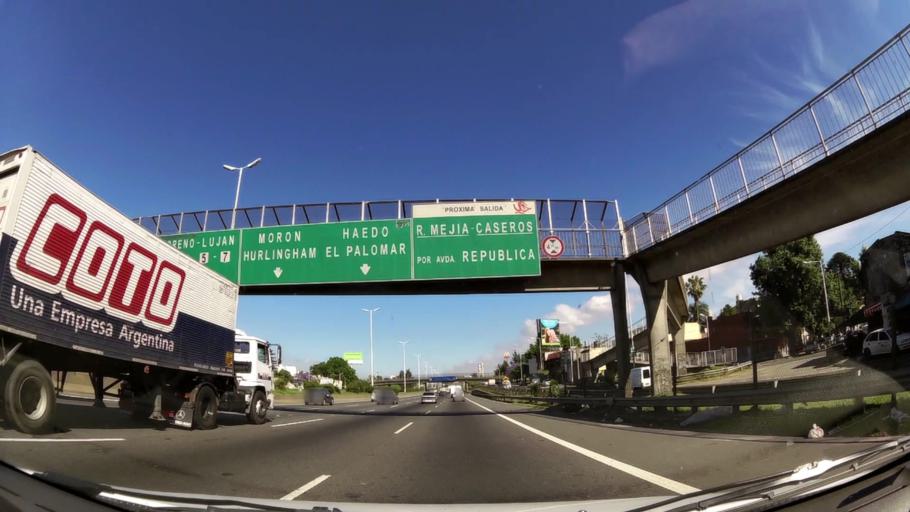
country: AR
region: Buenos Aires
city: Caseros
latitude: -34.6324
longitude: -58.5432
